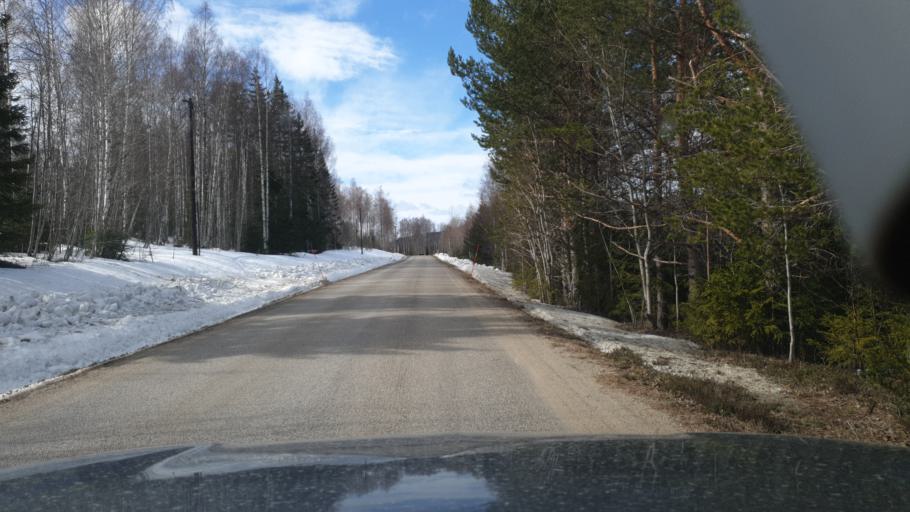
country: SE
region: Gaevleborg
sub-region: Ljusdals Kommun
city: Farila
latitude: 61.8425
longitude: 15.9090
